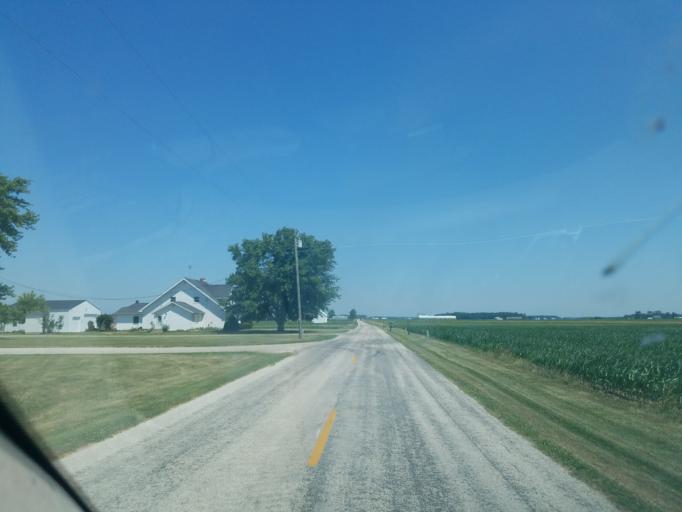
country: US
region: Ohio
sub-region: Mercer County
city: Rockford
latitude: 40.6242
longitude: -84.7085
